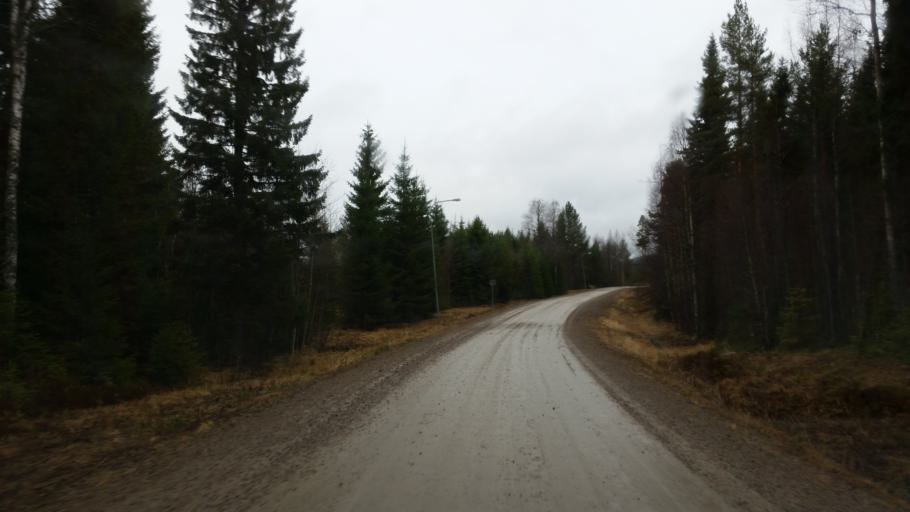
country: SE
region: Vaesternorrland
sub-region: Ange Kommun
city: Ange
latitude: 62.1441
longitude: 15.6612
